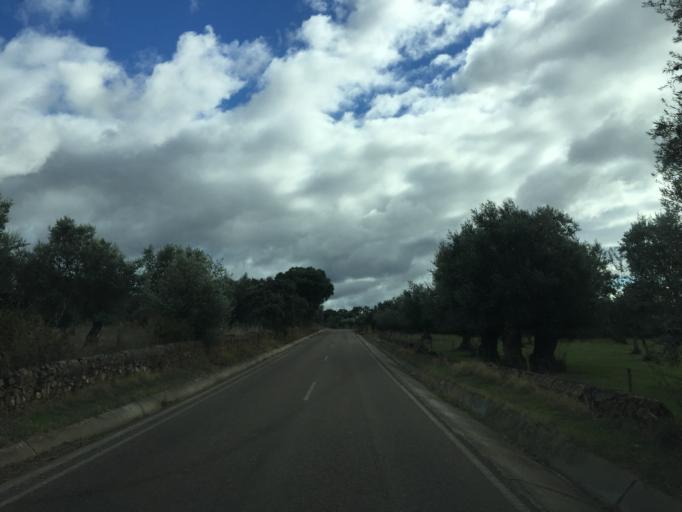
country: PT
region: Portalegre
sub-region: Alter do Chao
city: Alter do Chao
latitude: 39.2186
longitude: -7.6707
